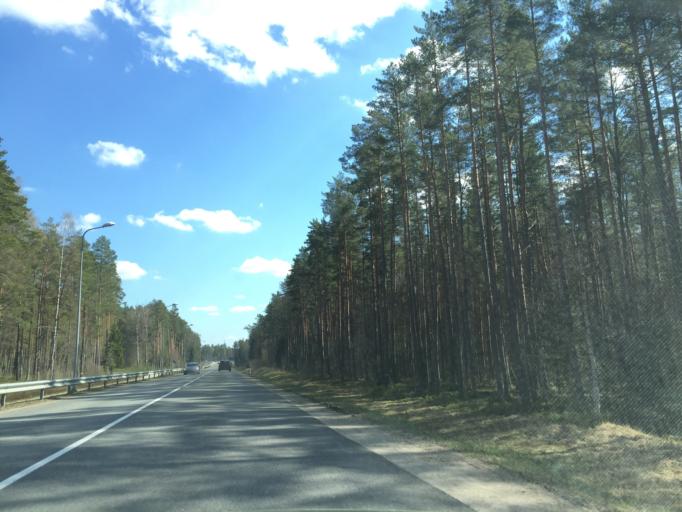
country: LV
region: Saulkrastu
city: Saulkrasti
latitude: 57.2488
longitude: 24.4157
